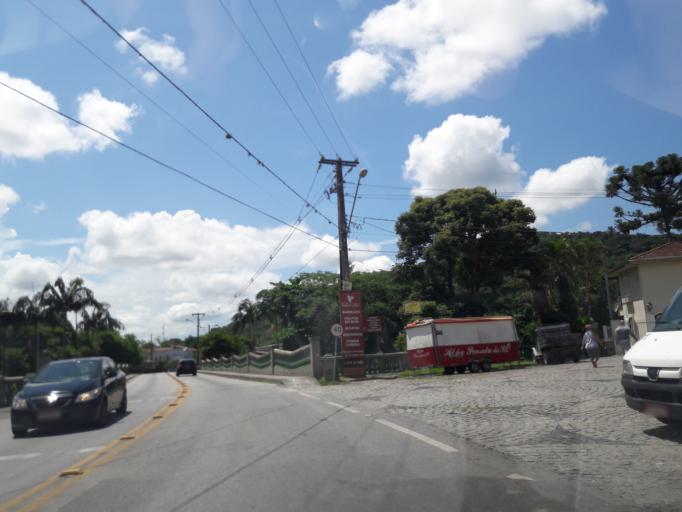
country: BR
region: Parana
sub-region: Antonina
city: Antonina
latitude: -25.4780
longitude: -48.8302
